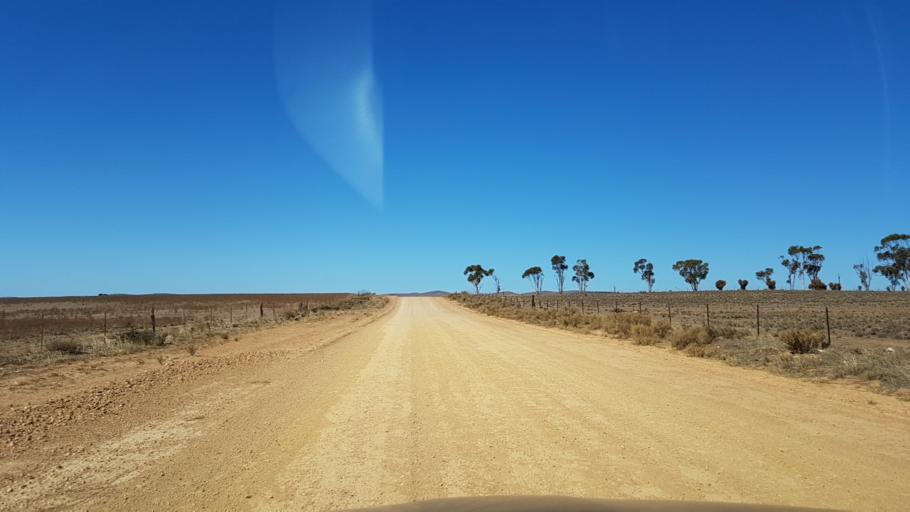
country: AU
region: South Australia
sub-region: Peterborough
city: Peterborough
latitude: -32.9907
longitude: 138.8432
